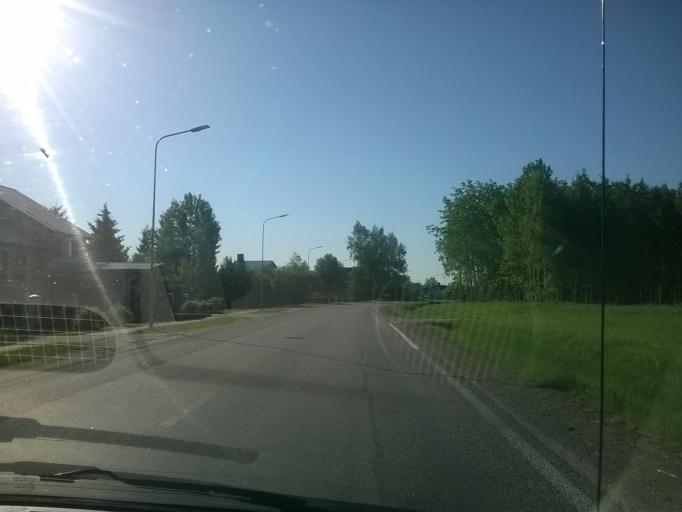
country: LV
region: Valkas Rajons
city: Valka
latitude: 57.7726
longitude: 25.9965
